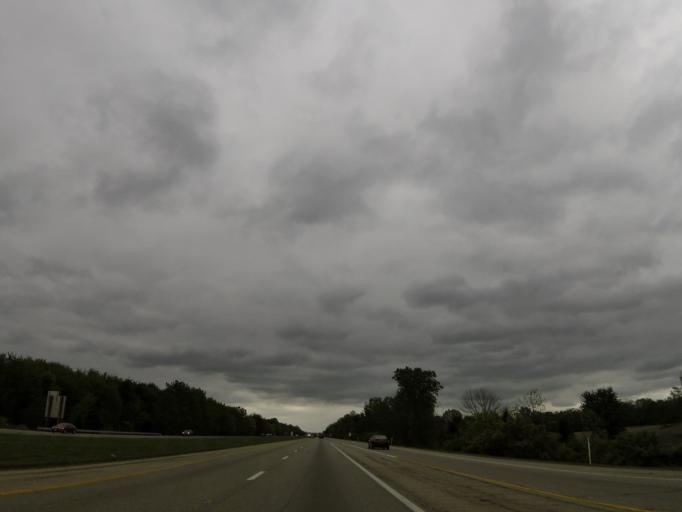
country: US
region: Ohio
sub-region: Warren County
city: Lebanon
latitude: 39.4130
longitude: -84.1483
